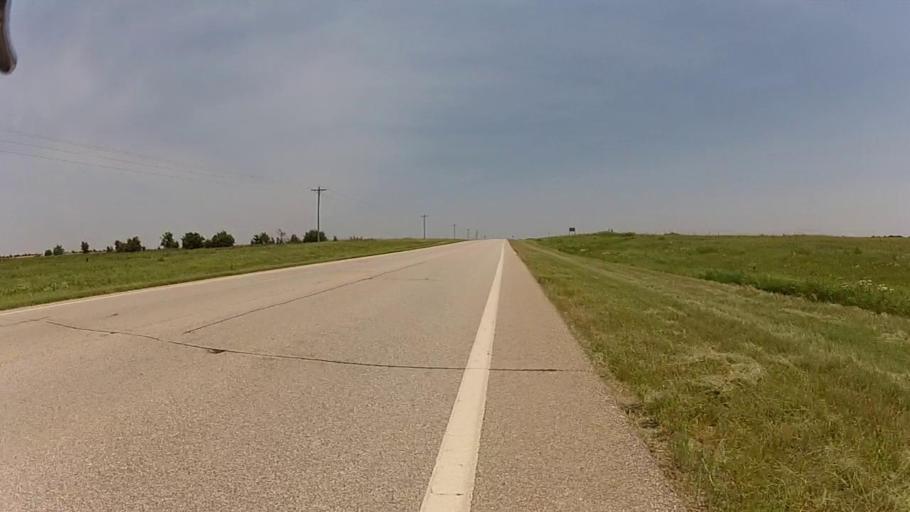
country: US
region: Kansas
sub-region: Cowley County
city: Arkansas City
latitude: 37.0569
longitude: -97.2255
